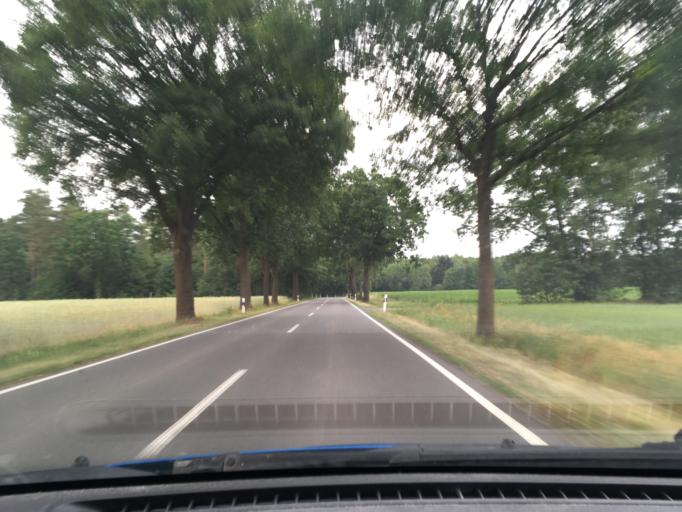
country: DE
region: Lower Saxony
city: Bad Fallingbostel
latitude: 52.8439
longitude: 9.6499
